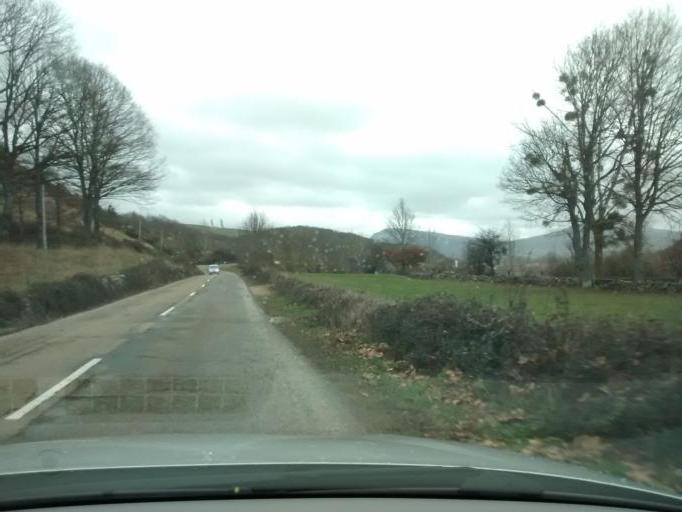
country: ES
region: Castille and Leon
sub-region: Provincia de Burgos
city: Espinosa de los Monteros
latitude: 43.0912
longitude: -3.5596
